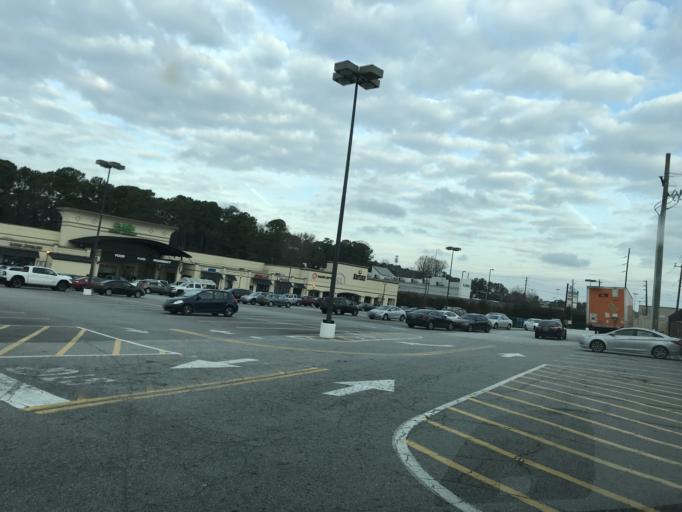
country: US
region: Georgia
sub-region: DeKalb County
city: Tucker
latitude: 33.8469
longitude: -84.2557
